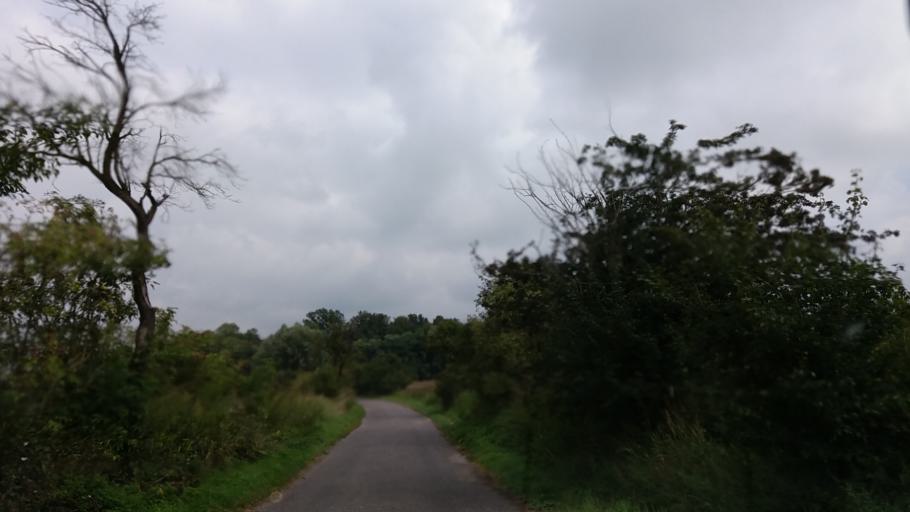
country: PL
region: West Pomeranian Voivodeship
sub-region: Powiat choszczenski
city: Krzecin
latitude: 53.1078
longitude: 15.4933
